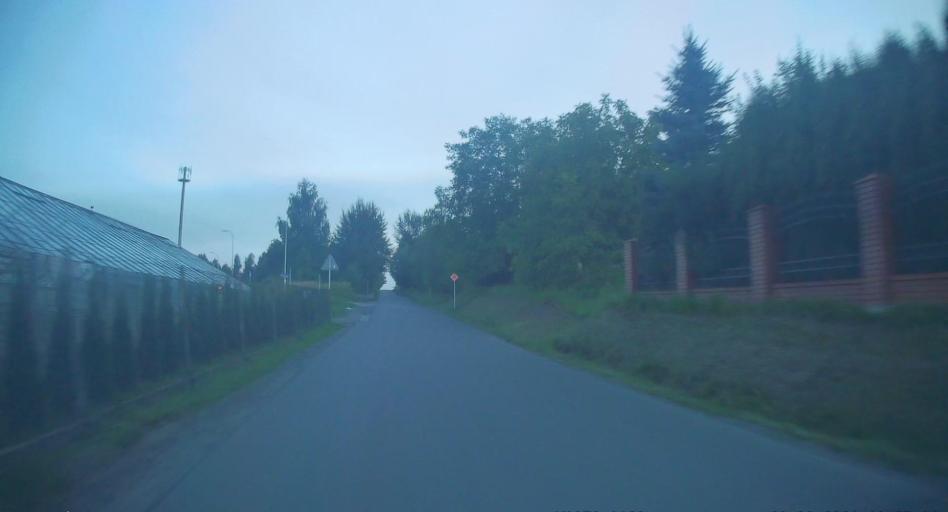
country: PL
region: Subcarpathian Voivodeship
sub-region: Rzeszow
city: Przybyszowka
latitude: 50.0490
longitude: 21.9456
